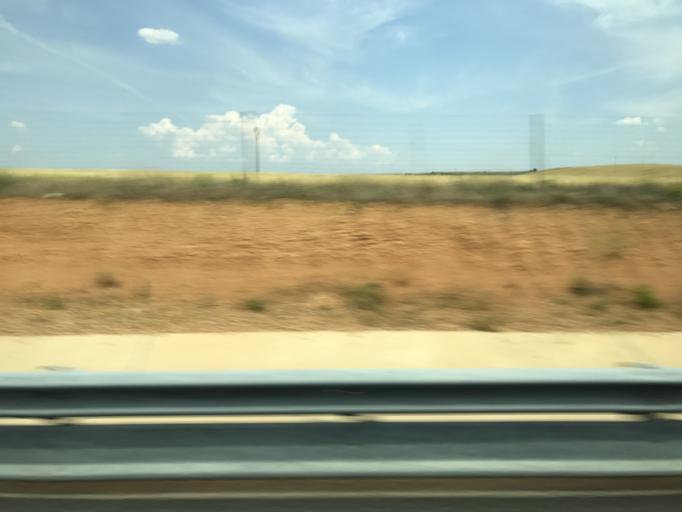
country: ES
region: Castille and Leon
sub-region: Provincia de Burgos
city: Fontioso
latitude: 41.9149
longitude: -3.7486
